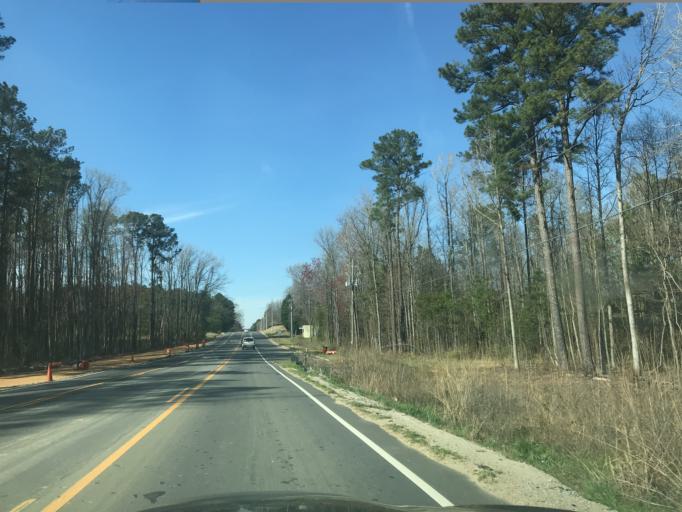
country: US
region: North Carolina
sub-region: Wake County
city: Fuquay-Varina
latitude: 35.5777
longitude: -78.7563
